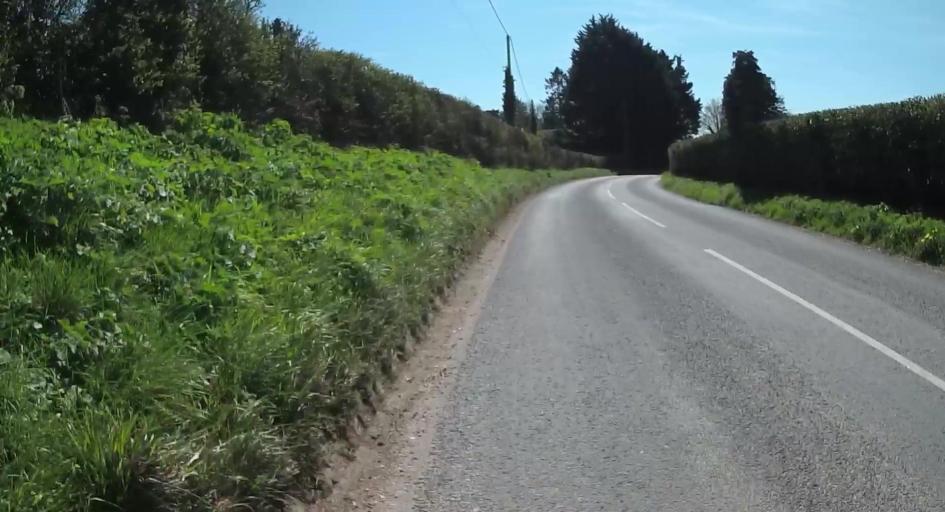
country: GB
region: England
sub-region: Hampshire
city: Winchester
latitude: 51.1064
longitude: -1.3879
